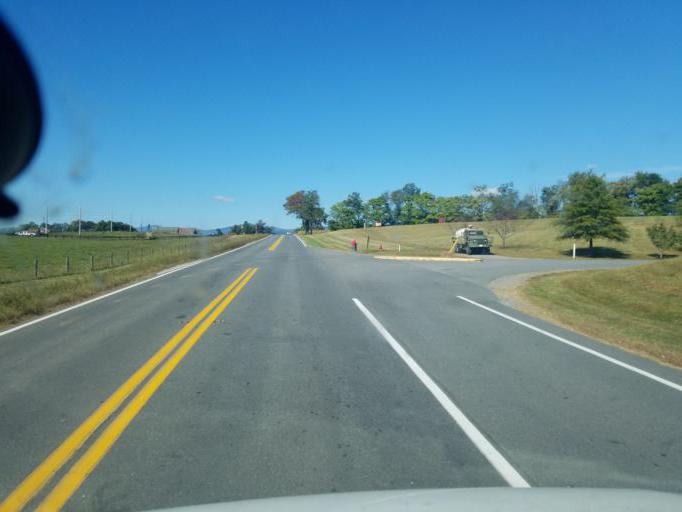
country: US
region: Virginia
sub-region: Madison County
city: Madison
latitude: 38.3480
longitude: -78.2917
